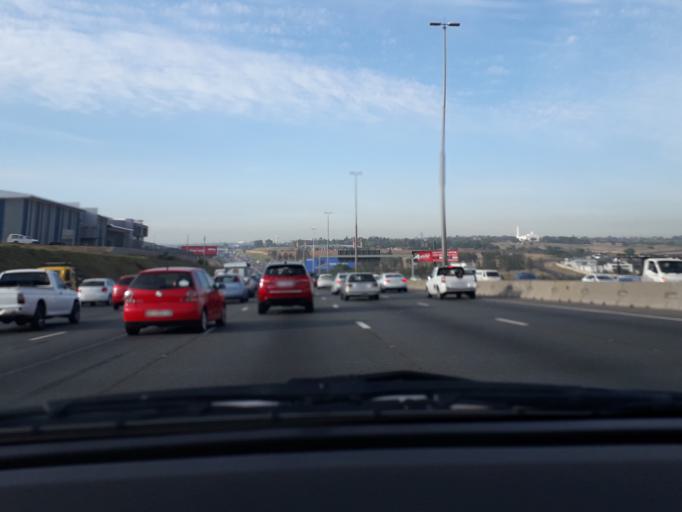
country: ZA
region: Gauteng
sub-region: City of Johannesburg Metropolitan Municipality
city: Midrand
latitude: -26.0245
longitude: 28.1114
